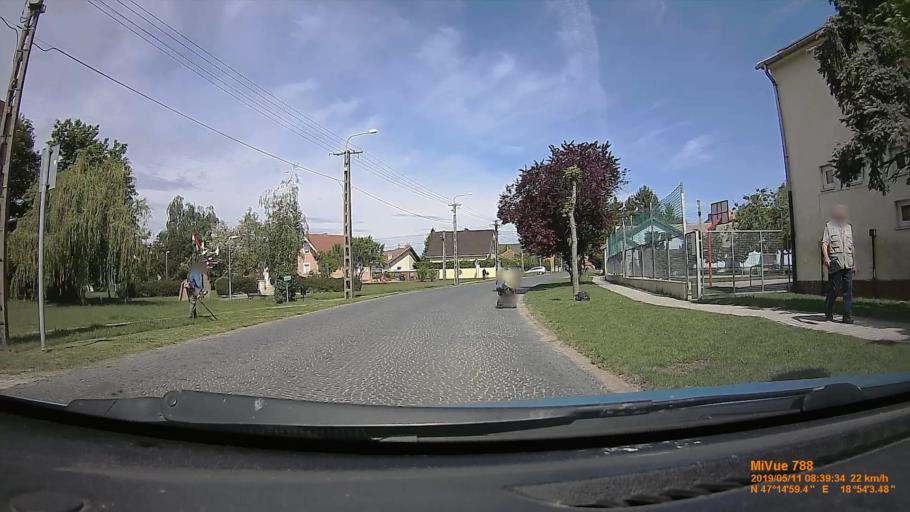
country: HU
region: Fejer
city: Ercsi
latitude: 47.2499
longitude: 18.9009
